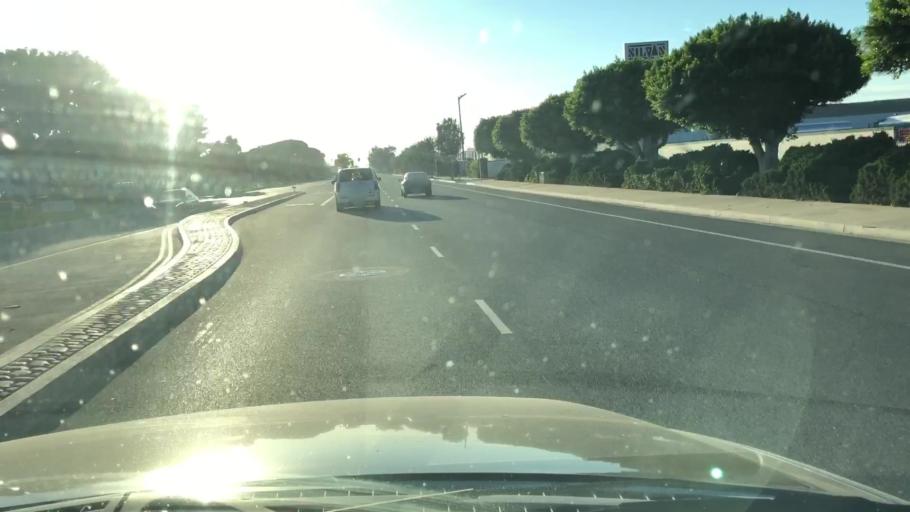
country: US
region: California
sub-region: Ventura County
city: Oxnard
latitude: 34.1902
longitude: -119.1615
